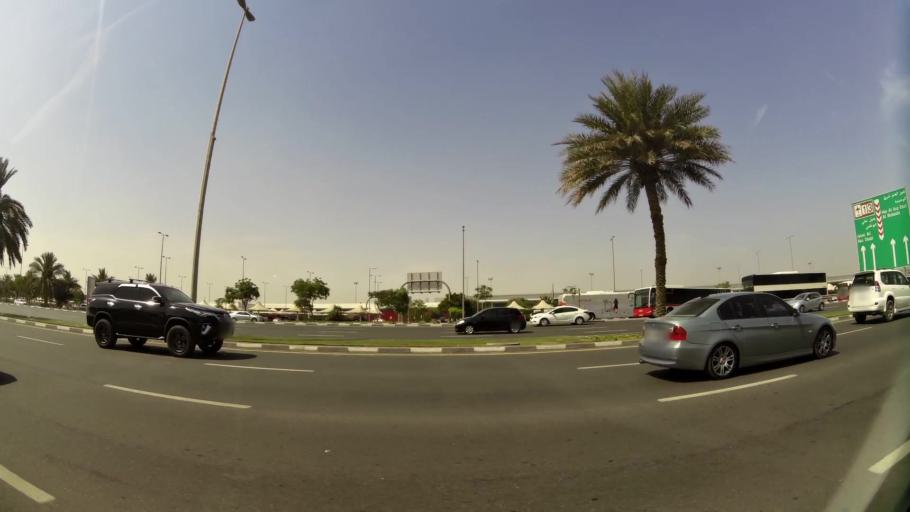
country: AE
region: Ash Shariqah
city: Sharjah
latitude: 25.2683
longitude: 55.3565
